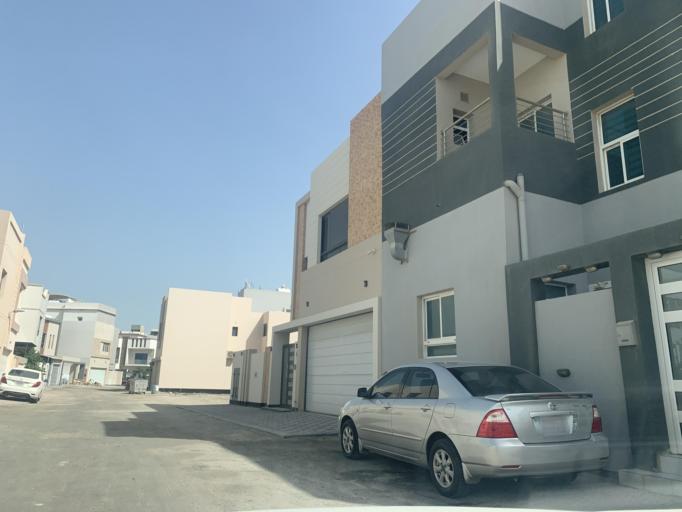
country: BH
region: Northern
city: Sitrah
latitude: 26.1721
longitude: 50.6266
